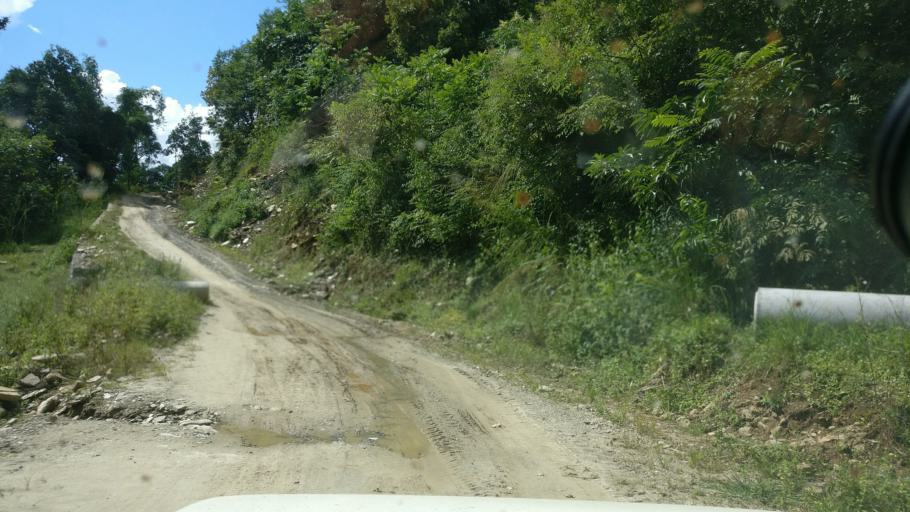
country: NP
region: Western Region
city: Baglung
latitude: 28.2605
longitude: 83.6527
